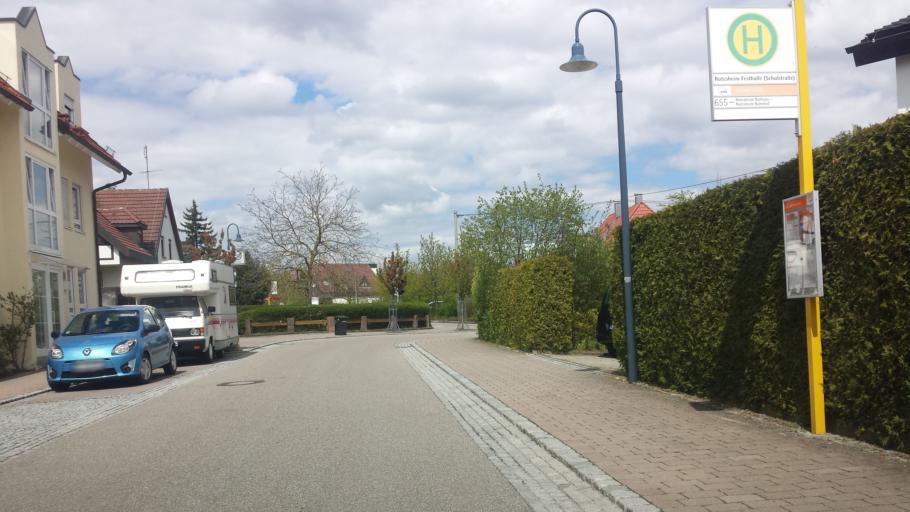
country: DE
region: Baden-Wuerttemberg
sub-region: Regierungsbezirk Stuttgart
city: Rutesheim
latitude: 48.8120
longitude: 8.9426
